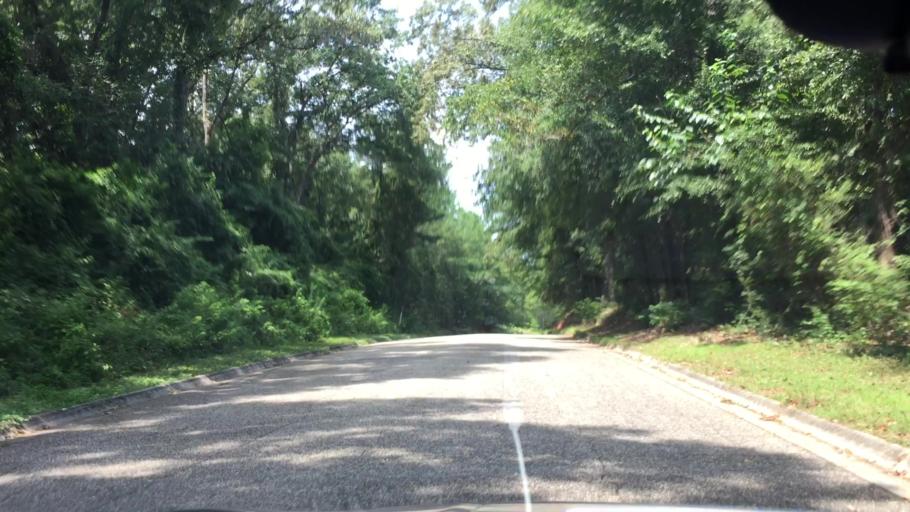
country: US
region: Alabama
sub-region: Coffee County
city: Enterprise
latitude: 31.3356
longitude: -85.8125
